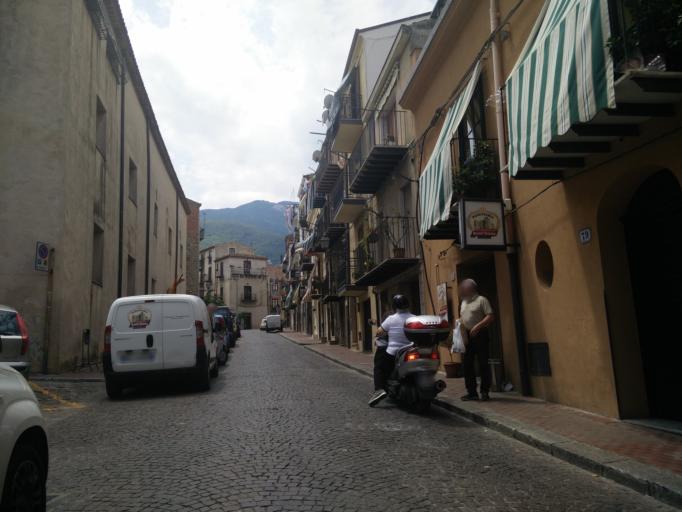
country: IT
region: Sicily
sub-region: Palermo
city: Castelbuono
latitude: 37.9313
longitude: 14.0866
